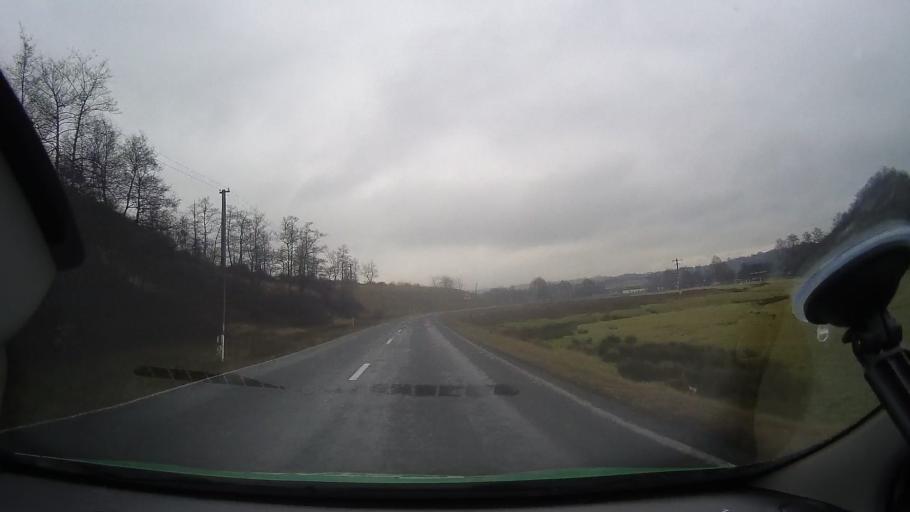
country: RO
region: Arad
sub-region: Comuna Varfurile
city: Varfurile
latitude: 46.3227
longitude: 22.4748
